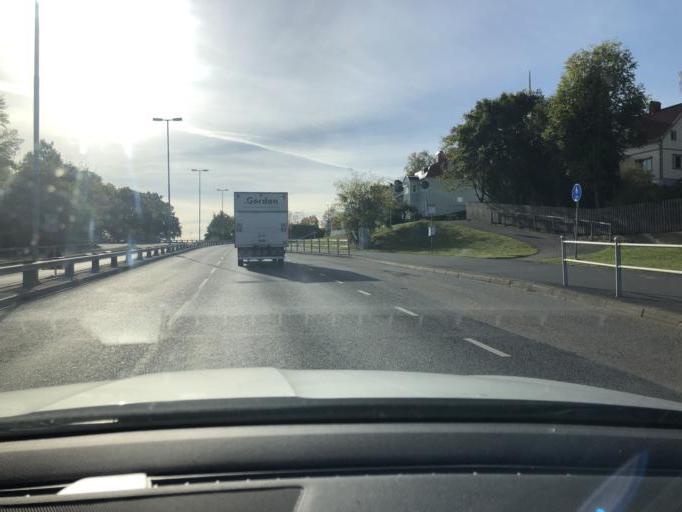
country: SE
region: Joenkoeping
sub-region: Jonkopings Kommun
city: Jonkoping
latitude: 57.7750
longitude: 14.1408
